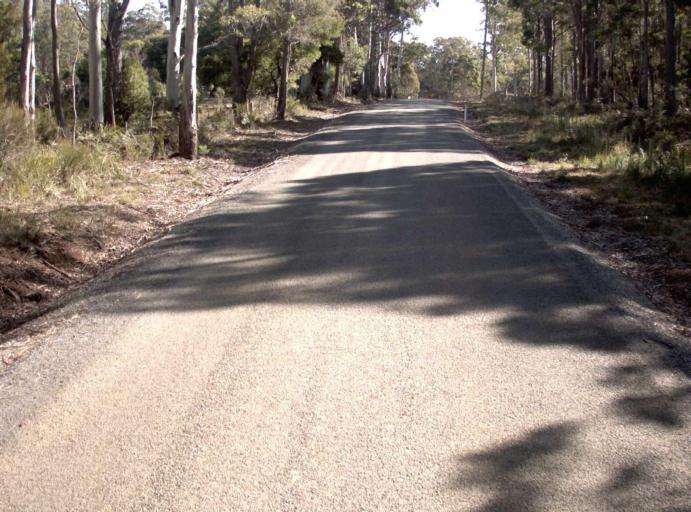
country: AU
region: Tasmania
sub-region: Launceston
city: Mayfield
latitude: -41.3155
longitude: 147.2052
